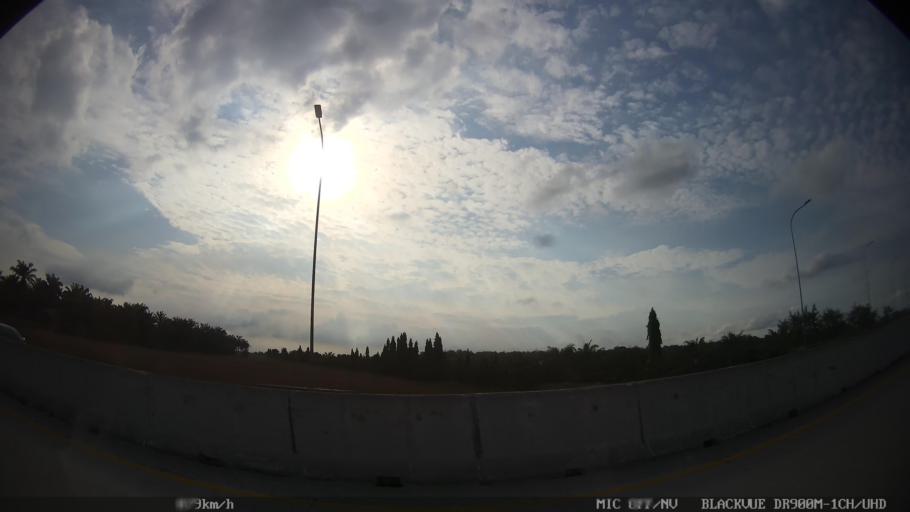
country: ID
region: North Sumatra
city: Medan
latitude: 3.6373
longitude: 98.6374
